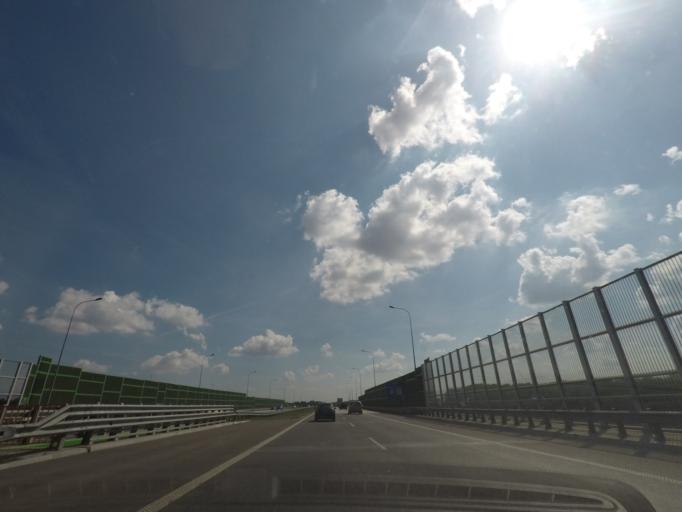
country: PL
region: Lodz Voivodeship
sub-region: Powiat zgierski
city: Strykow
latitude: 51.8467
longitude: 19.6598
